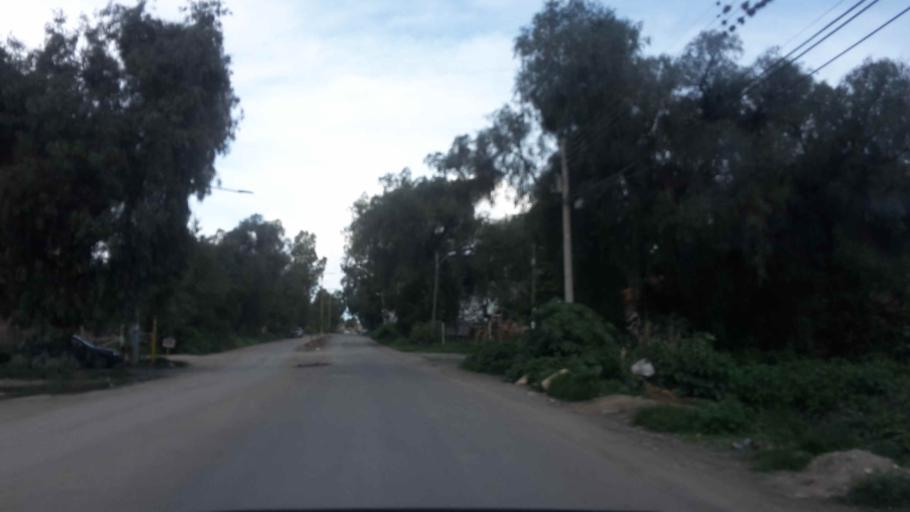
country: BO
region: Cochabamba
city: Cochabamba
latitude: -17.3988
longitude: -66.2704
